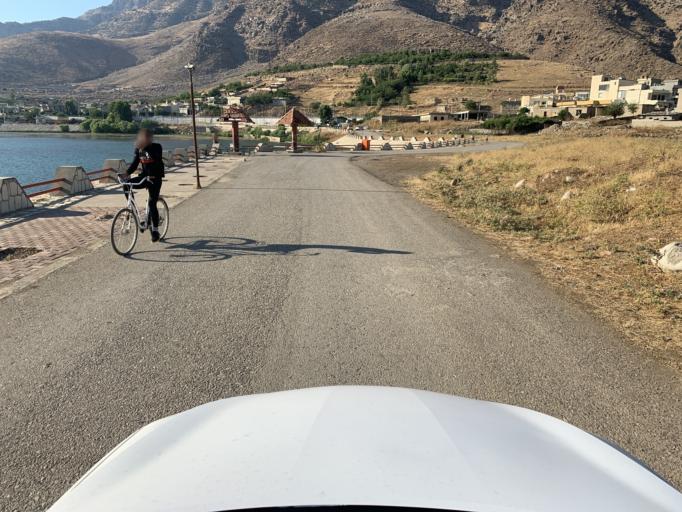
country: IQ
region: As Sulaymaniyah
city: Raniye
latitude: 36.2727
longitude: 44.7558
